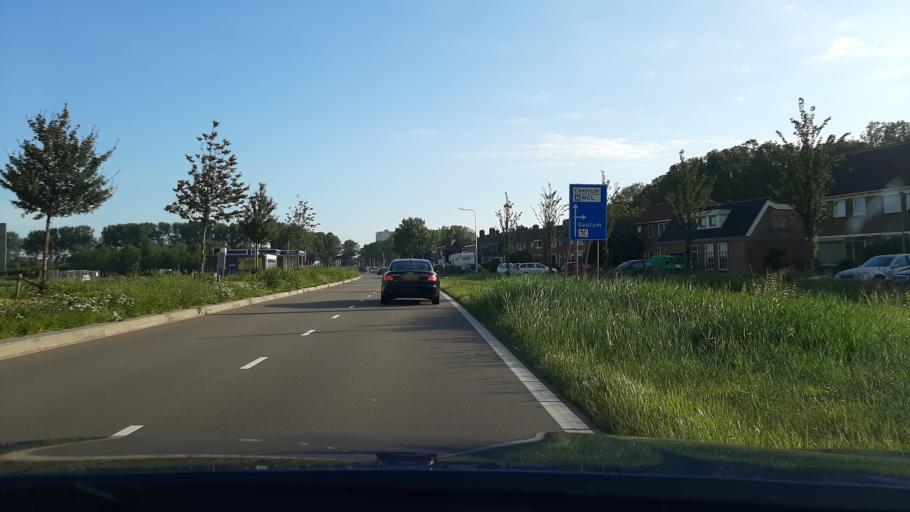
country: NL
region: Friesland
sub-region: Gemeente Leeuwarden
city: Goutum
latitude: 53.1762
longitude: 5.7949
